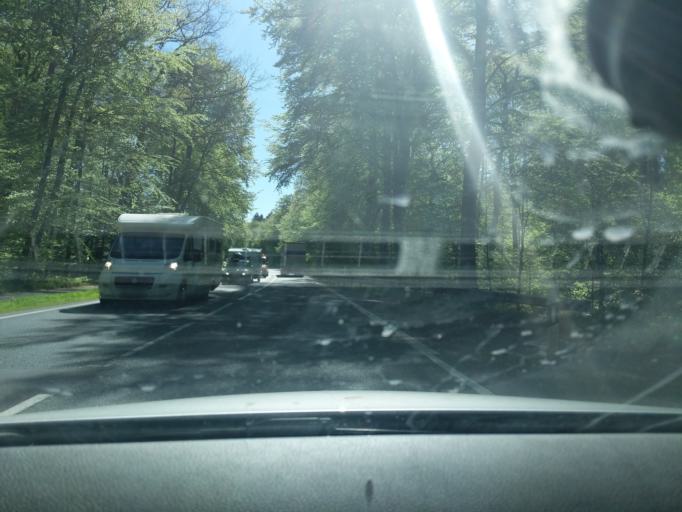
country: DE
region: Lower Saxony
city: Buxtehude
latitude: 53.4748
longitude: 9.6504
